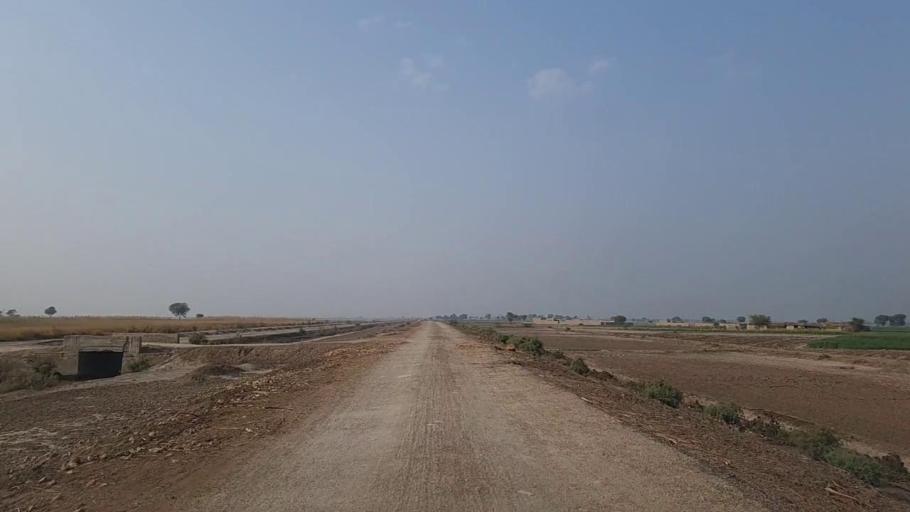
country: PK
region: Sindh
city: Nawabshah
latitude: 26.3315
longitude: 68.4756
